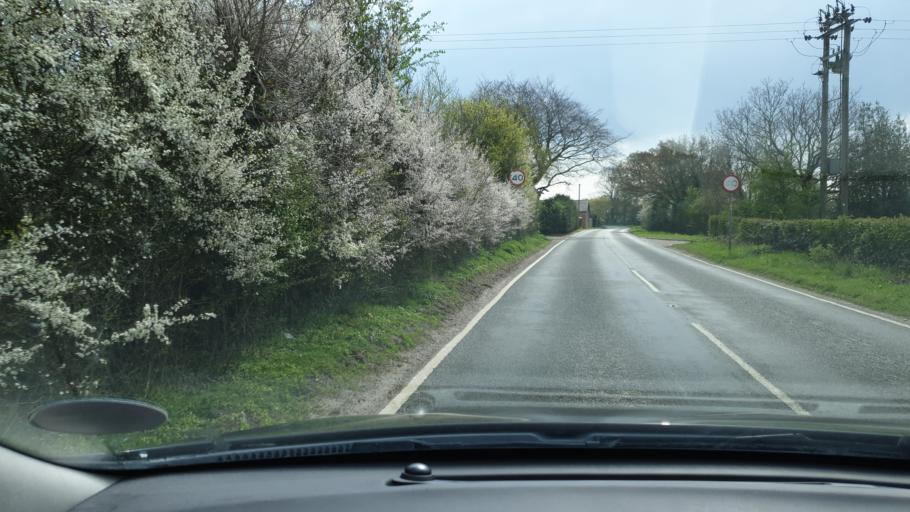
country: GB
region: England
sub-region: Essex
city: Alresford
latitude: 51.9146
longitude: 0.9954
